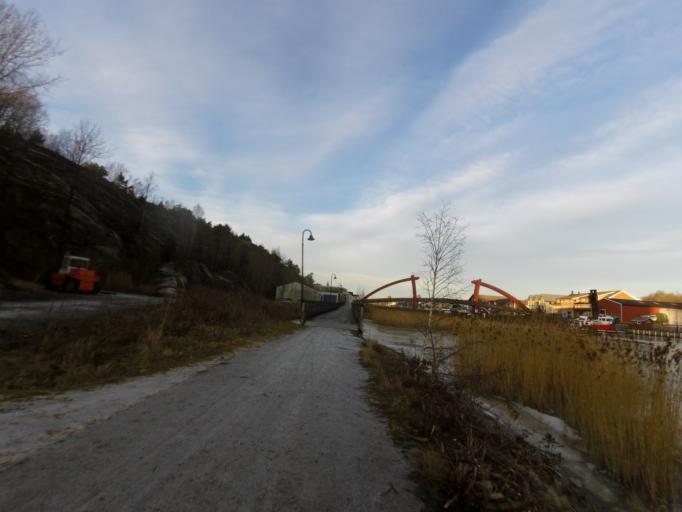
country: NO
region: Ostfold
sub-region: Fredrikstad
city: Fredrikstad
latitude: 59.2215
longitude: 10.9146
